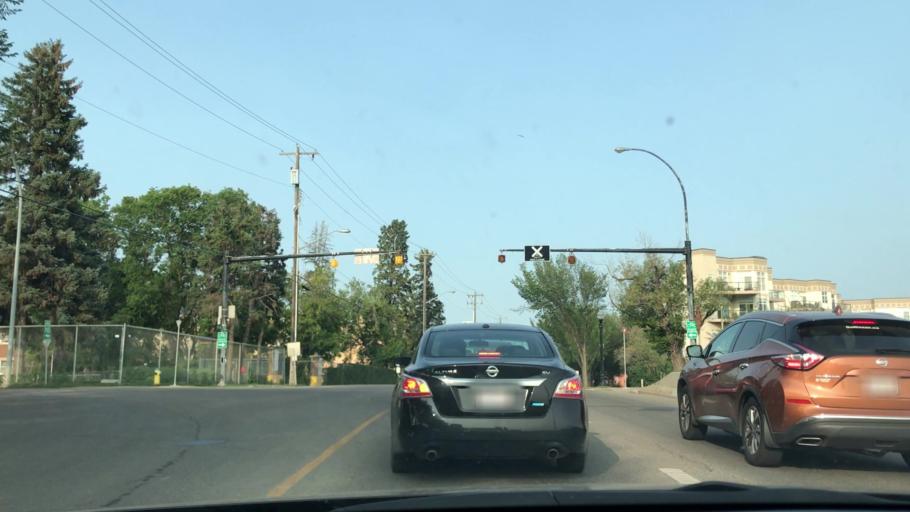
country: CA
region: Alberta
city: Edmonton
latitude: 53.5429
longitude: -113.4807
